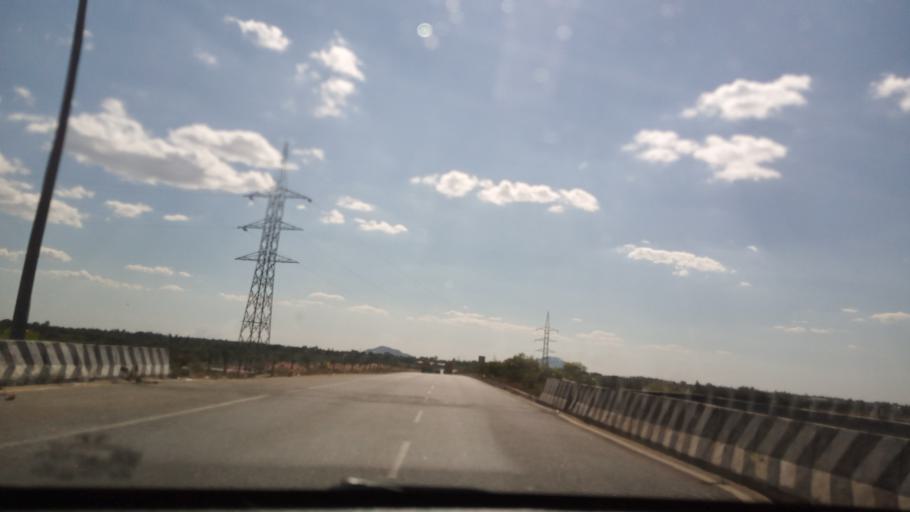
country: IN
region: Karnataka
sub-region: Kolar
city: Mulbagal
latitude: 13.1531
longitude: 78.4022
